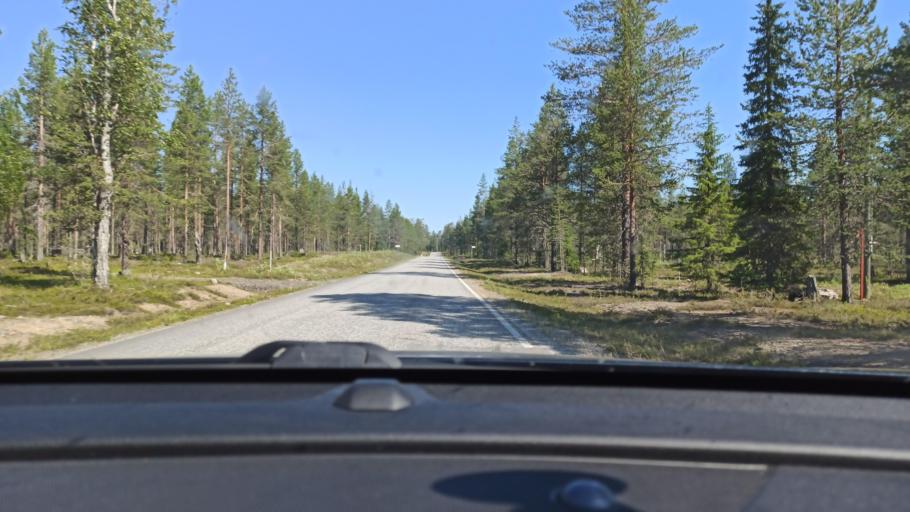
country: FI
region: Lapland
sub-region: Tunturi-Lappi
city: Kolari
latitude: 67.6551
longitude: 24.1639
